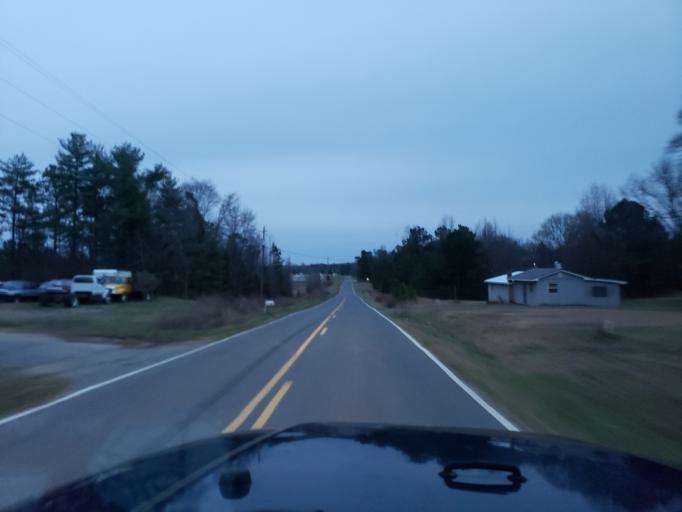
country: US
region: North Carolina
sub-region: Cleveland County
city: White Plains
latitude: 35.1766
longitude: -81.4131
